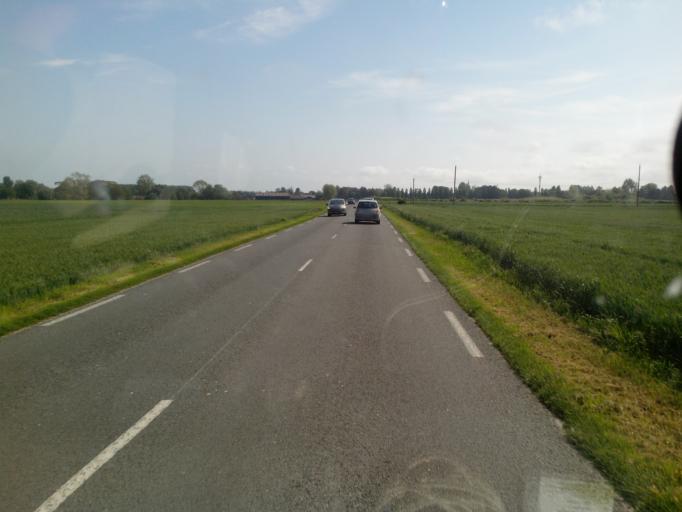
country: FR
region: Picardie
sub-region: Departement de la Somme
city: Quend
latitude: 50.3260
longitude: 1.6408
